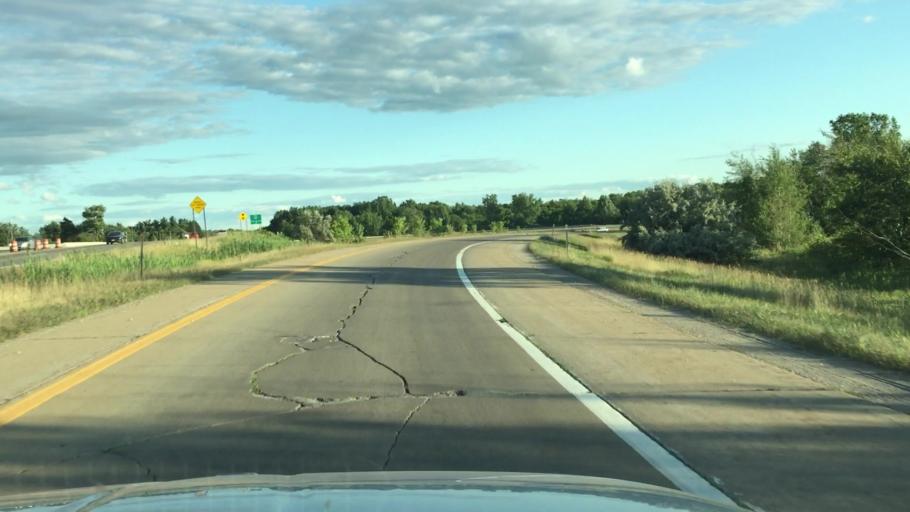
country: US
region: Michigan
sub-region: Lapeer County
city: Imlay City
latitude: 43.0028
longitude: -83.0716
